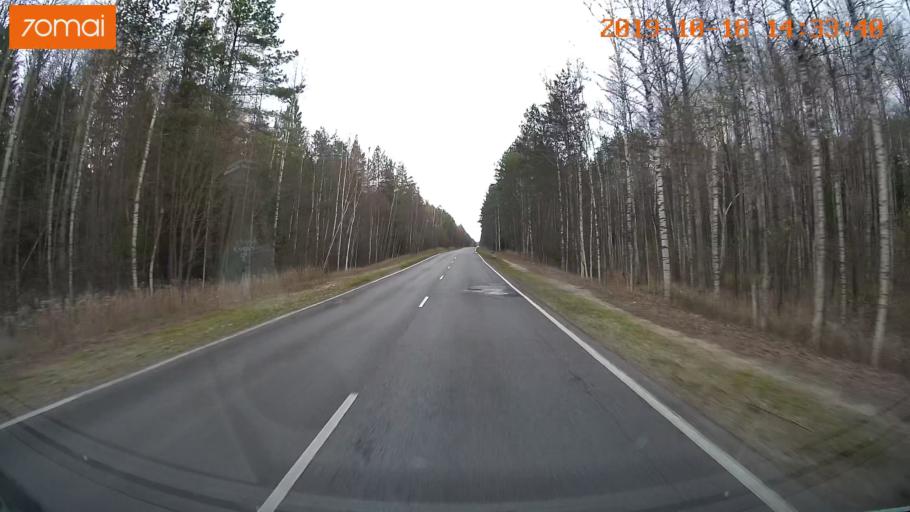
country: RU
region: Rjazan
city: Tuma
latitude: 55.2039
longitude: 40.6011
